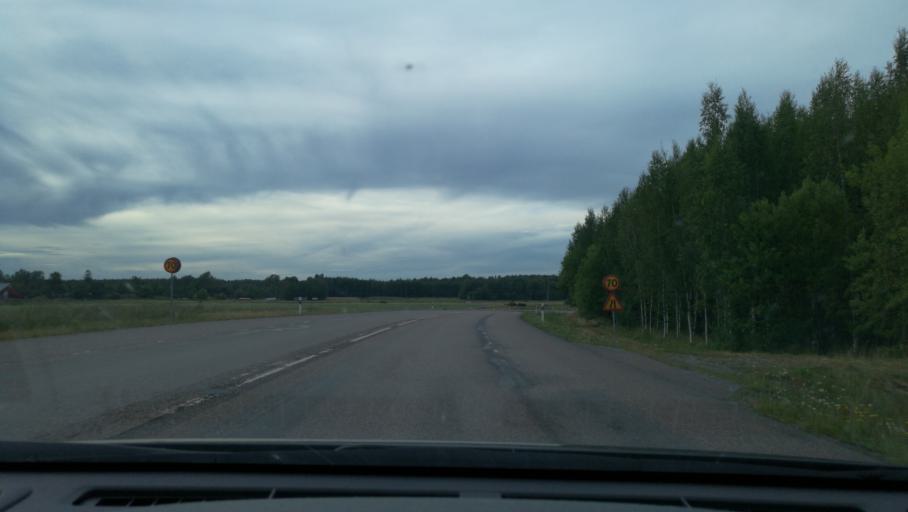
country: SE
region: Vaestmanland
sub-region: Kopings Kommun
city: Koping
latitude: 59.4816
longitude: 15.9860
